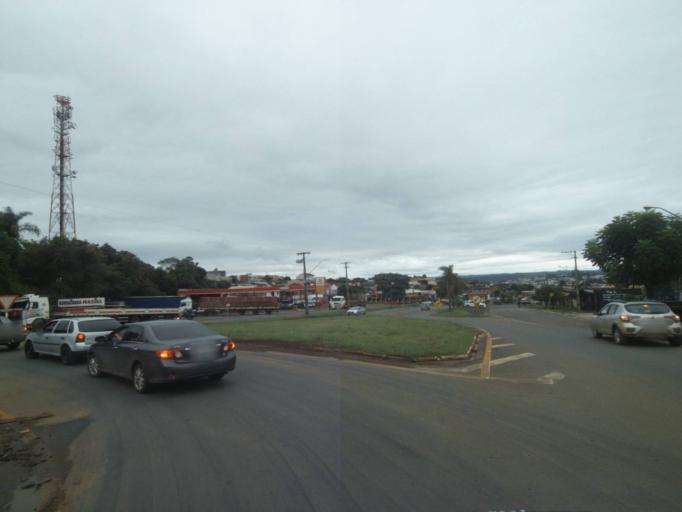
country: BR
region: Parana
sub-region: Telemaco Borba
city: Telemaco Borba
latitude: -24.3302
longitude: -50.6438
